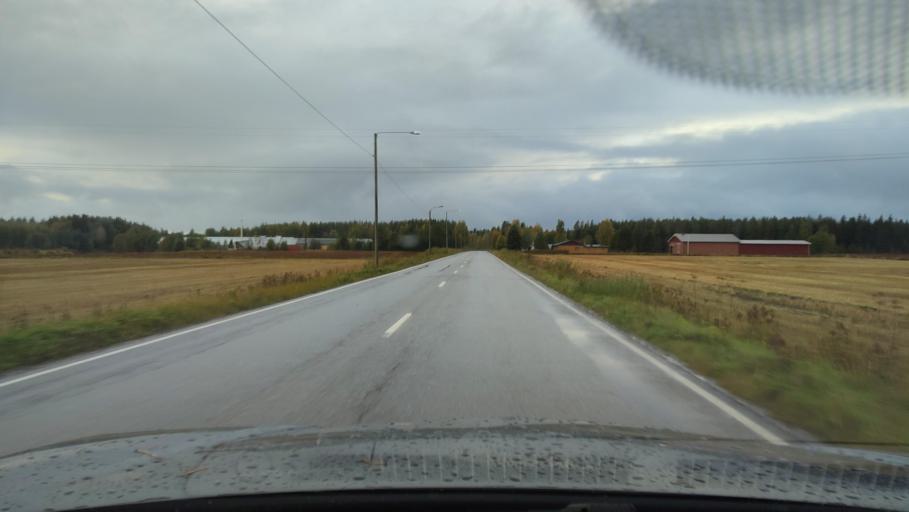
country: FI
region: Southern Ostrobothnia
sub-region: Suupohja
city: Karijoki
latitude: 62.2375
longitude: 21.6095
